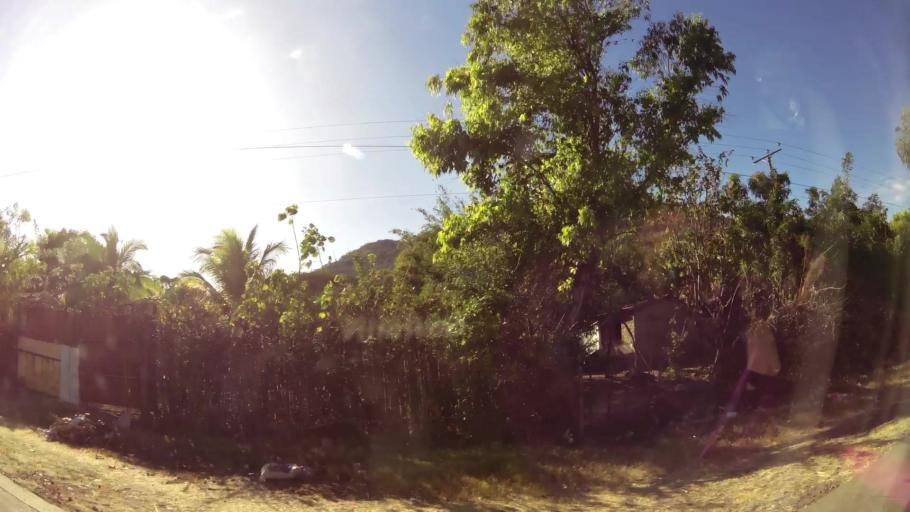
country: SV
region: Santa Ana
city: Santa Ana
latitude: 14.0517
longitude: -89.5161
